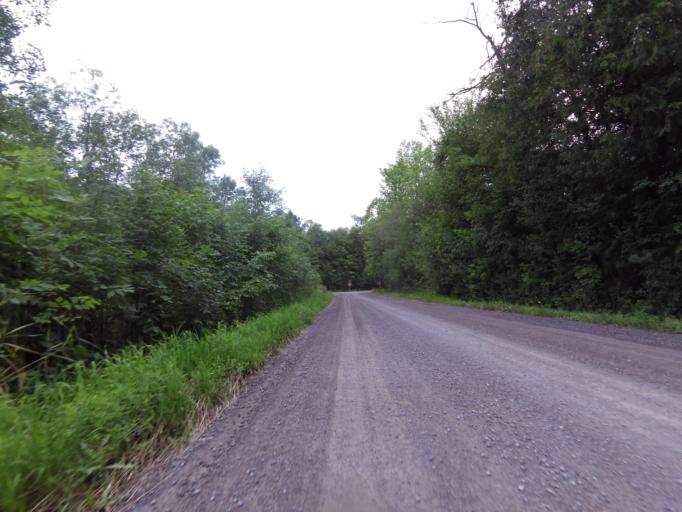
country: CA
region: Ontario
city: Carleton Place
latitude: 45.1457
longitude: -76.2257
